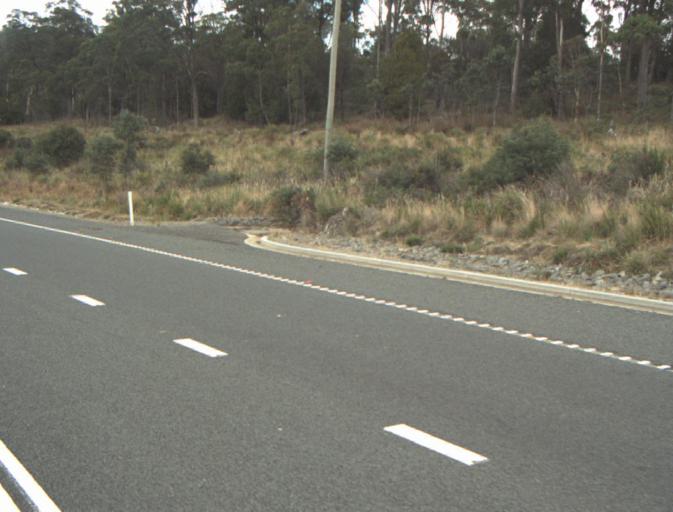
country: AU
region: Tasmania
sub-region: Launceston
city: Mayfield
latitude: -41.2589
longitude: 147.0263
